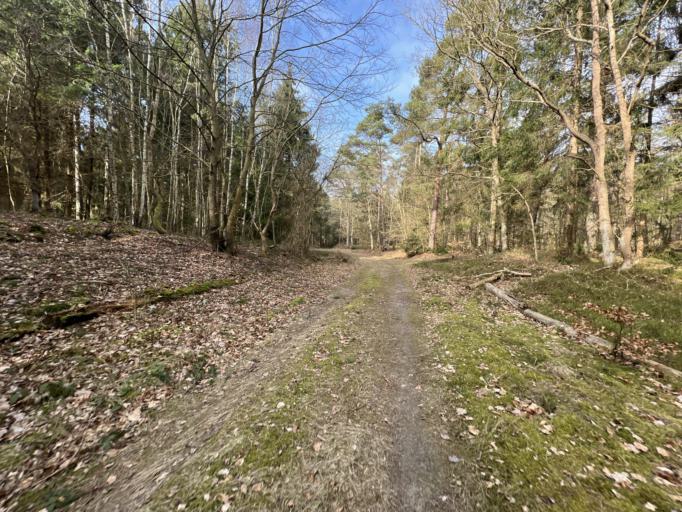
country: DE
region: Mecklenburg-Vorpommern
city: Sagard
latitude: 54.4784
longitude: 13.5616
